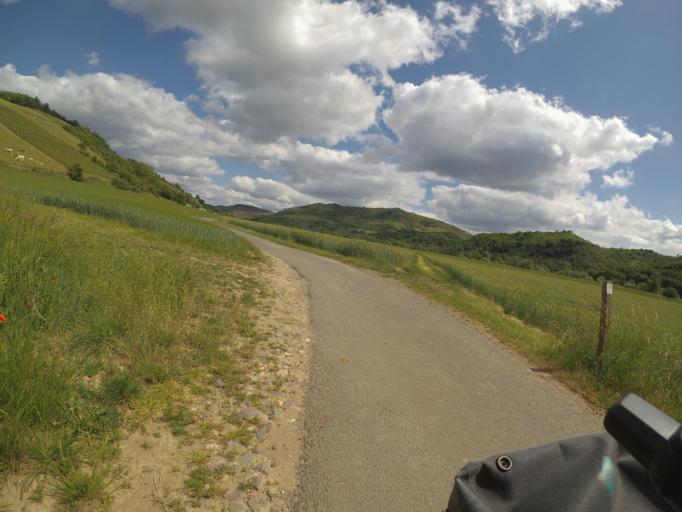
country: DE
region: Rheinland-Pfalz
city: Duchroth
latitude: 49.7810
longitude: 7.7158
